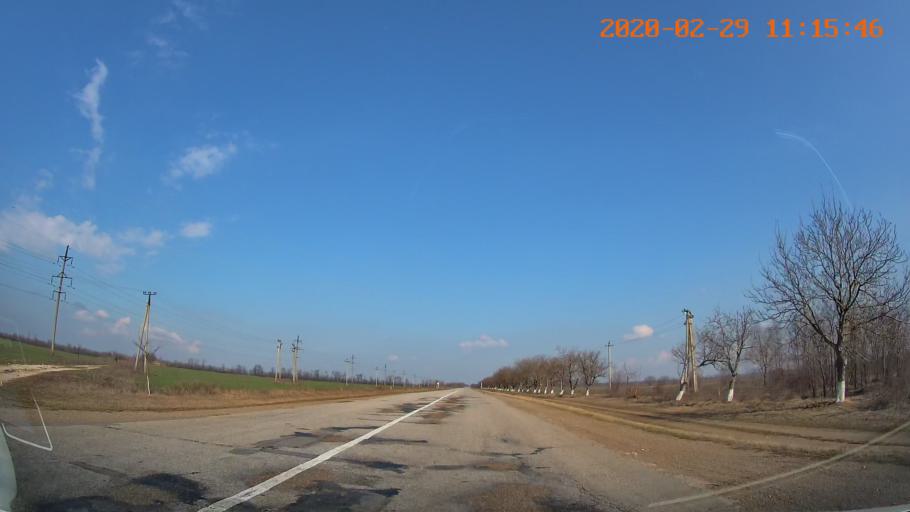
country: MD
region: Telenesti
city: Dubasari
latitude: 47.2992
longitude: 29.1660
